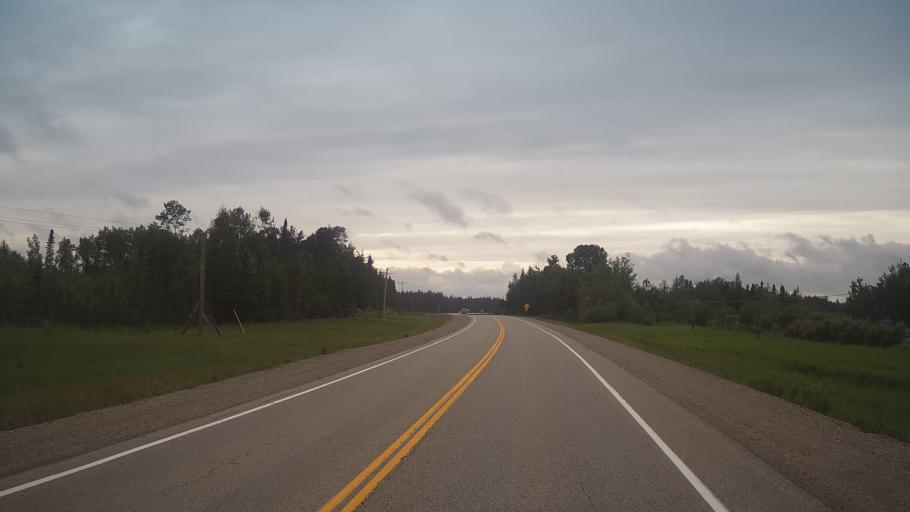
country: CA
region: Ontario
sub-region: Thunder Bay District
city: Thunder Bay
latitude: 48.8845
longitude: -89.9969
